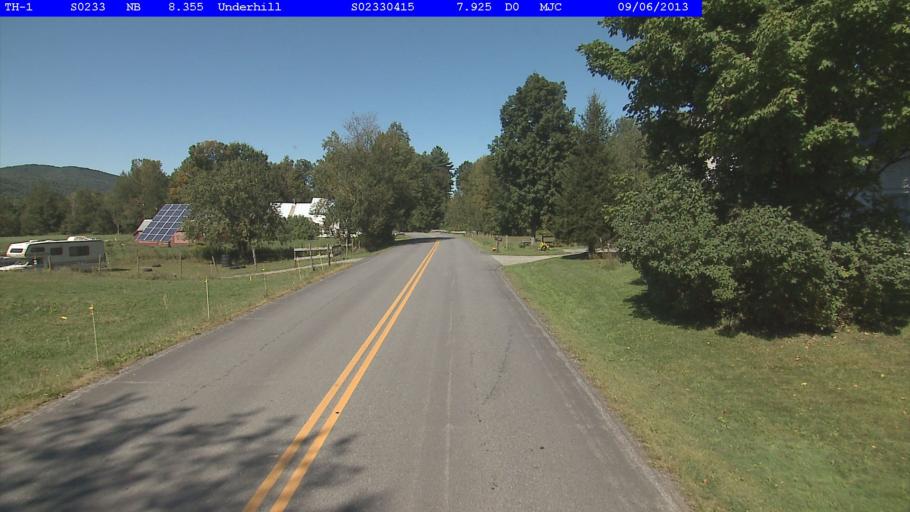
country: US
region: Vermont
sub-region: Chittenden County
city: Jericho
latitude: 44.5788
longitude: -72.8628
